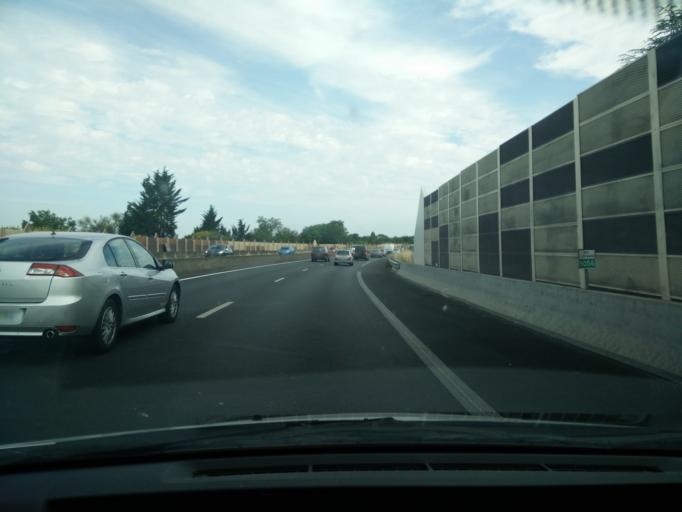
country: FR
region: Pays de la Loire
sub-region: Departement de Maine-et-Loire
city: Angers
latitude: 47.4588
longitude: -0.5178
